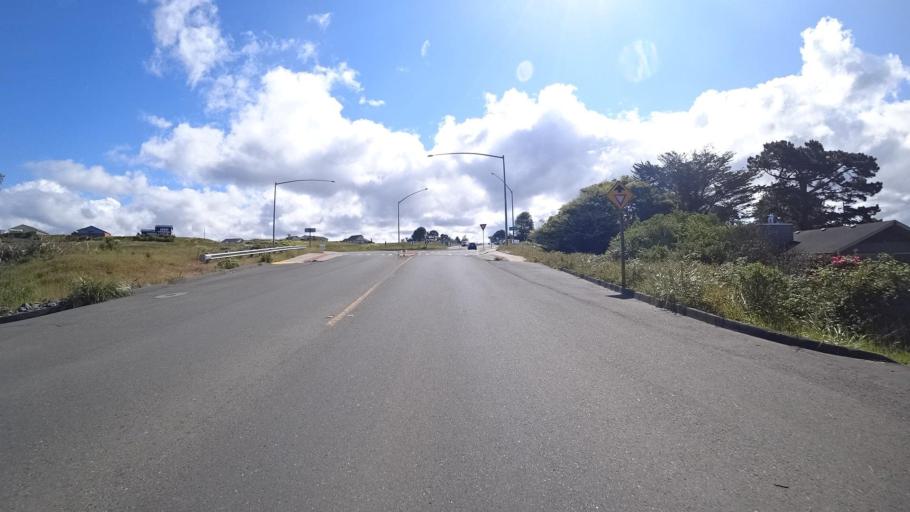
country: US
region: California
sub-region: Humboldt County
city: McKinleyville
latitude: 40.9340
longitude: -124.1124
